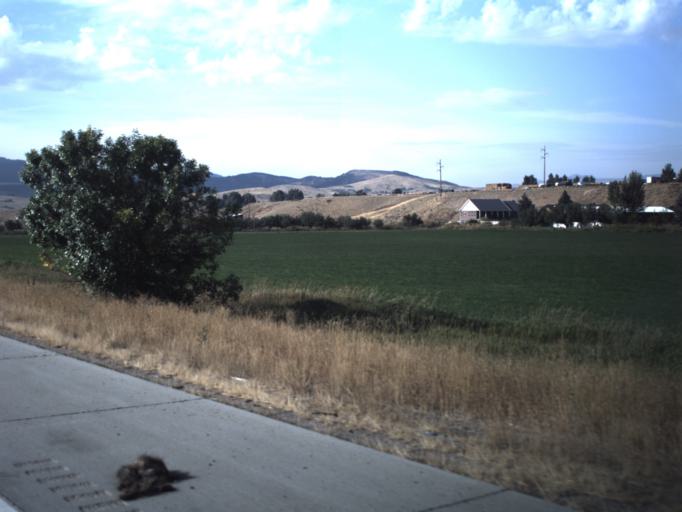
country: US
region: Utah
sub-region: Morgan County
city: Mountain Green
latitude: 41.1295
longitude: -111.7739
